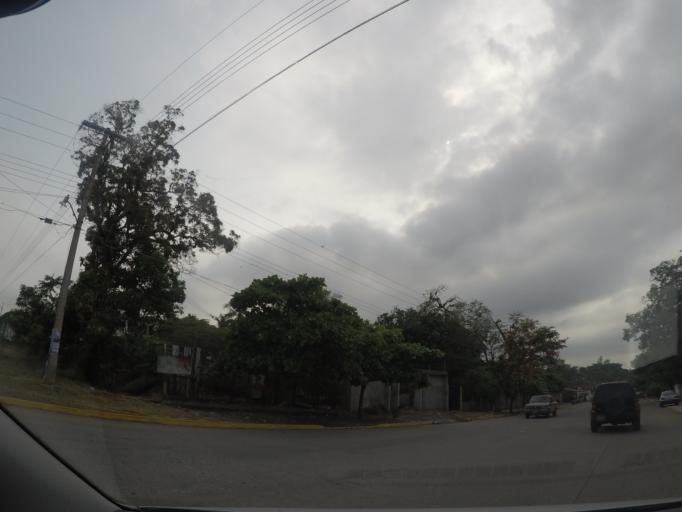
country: MX
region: Oaxaca
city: Matias Romero
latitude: 16.8744
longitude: -95.0465
